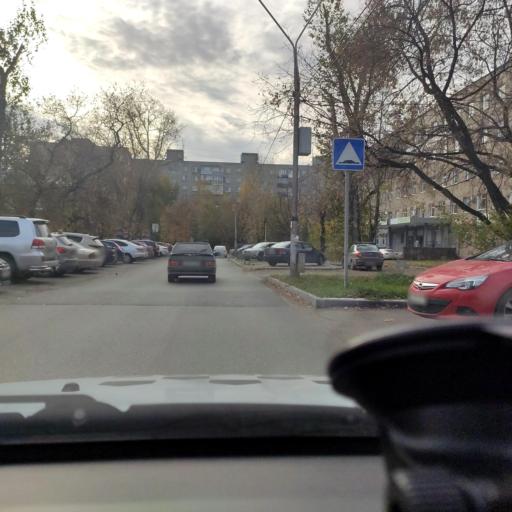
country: RU
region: Perm
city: Perm
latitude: 58.0113
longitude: 56.2137
